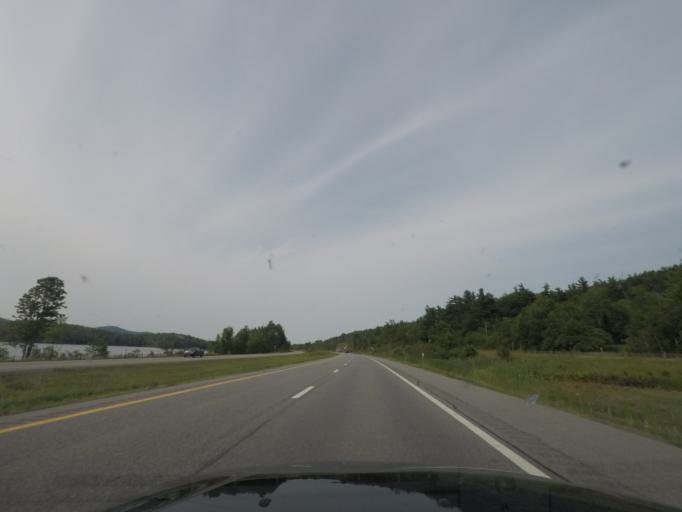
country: US
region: New York
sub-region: Essex County
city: Keeseville
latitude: 44.4258
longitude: -73.4922
